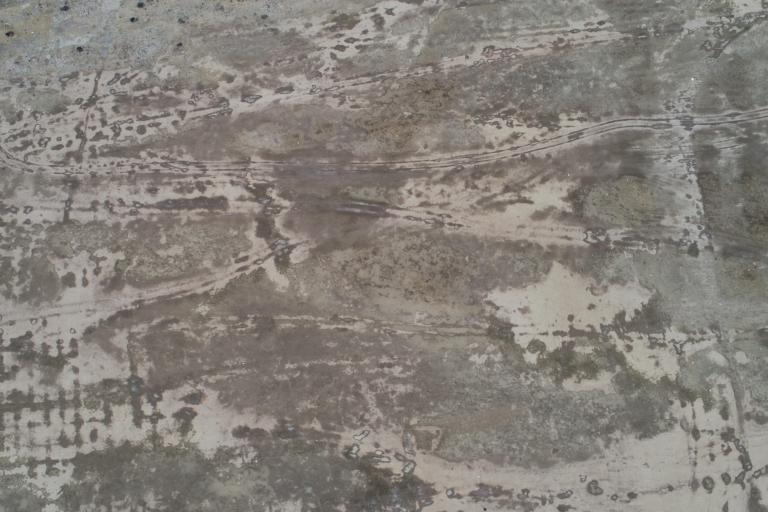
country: BO
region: La Paz
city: Achacachi
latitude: -16.0532
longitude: -68.6874
